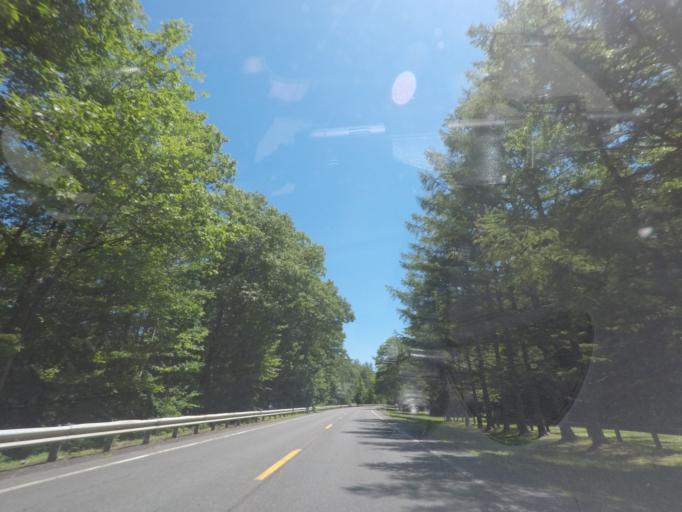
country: US
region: Massachusetts
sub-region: Hampshire County
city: Westhampton
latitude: 42.2449
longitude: -72.9179
